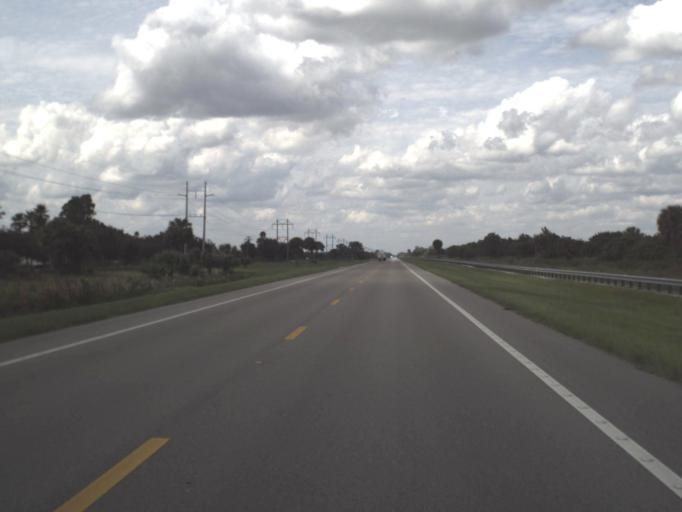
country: US
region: Florida
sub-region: Collier County
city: Immokalee
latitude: 26.3664
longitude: -81.3506
